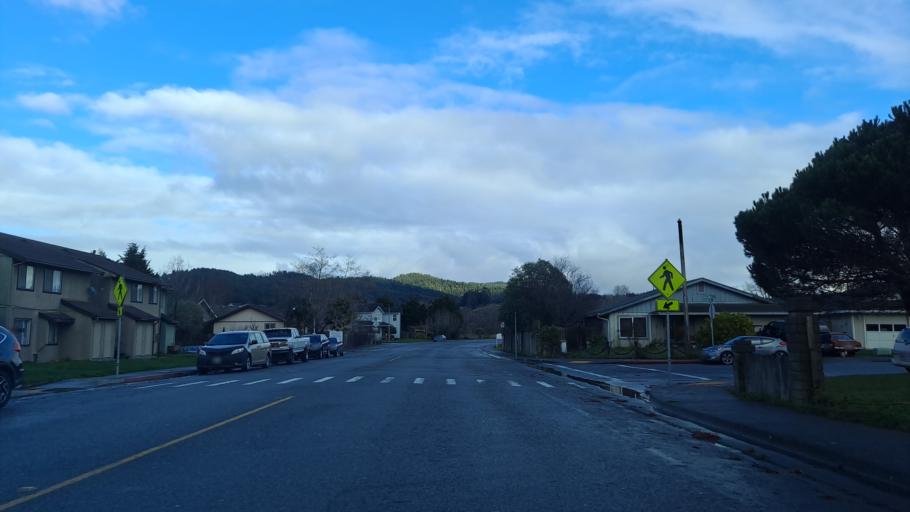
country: US
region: California
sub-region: Humboldt County
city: Fortuna
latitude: 40.5847
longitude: -124.1412
